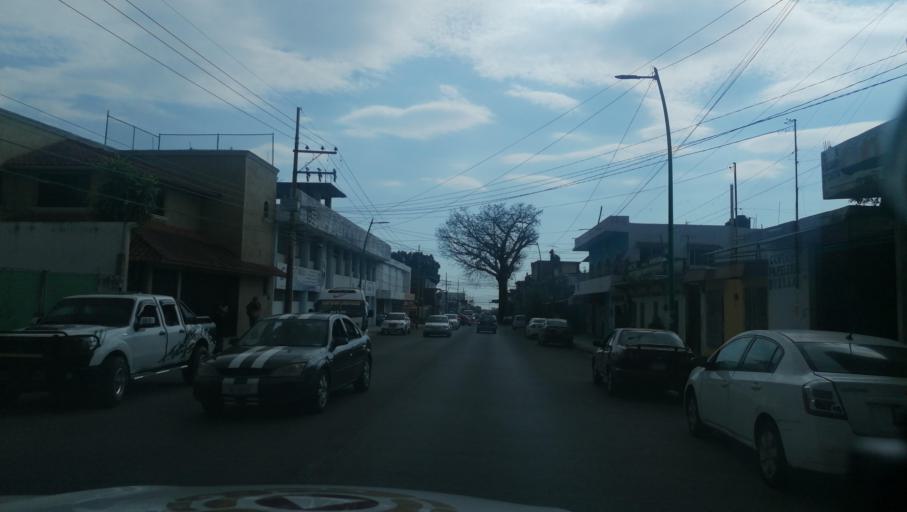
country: MX
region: Chiapas
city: Tapachula
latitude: 14.9202
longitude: -92.2558
